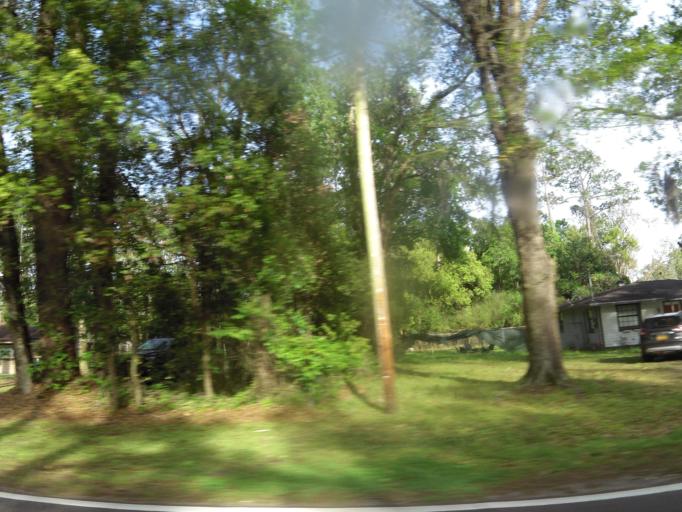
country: US
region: Florida
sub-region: Clay County
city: Bellair-Meadowbrook Terrace
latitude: 30.2395
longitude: -81.7646
